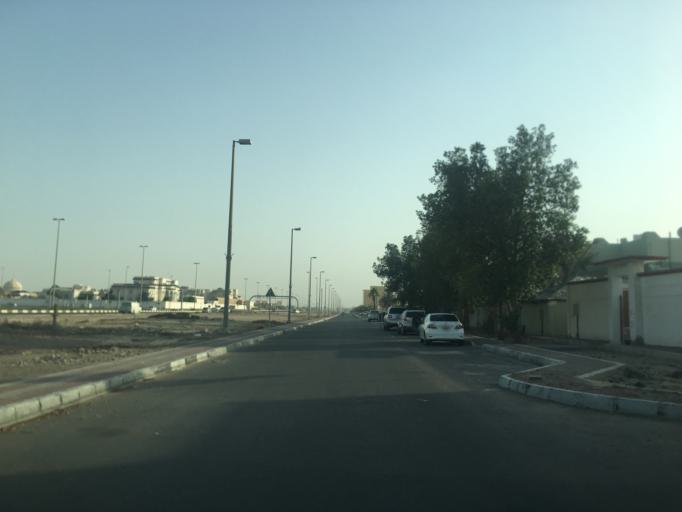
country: AE
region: Abu Dhabi
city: Abu Dhabi
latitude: 24.3085
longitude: 54.6405
